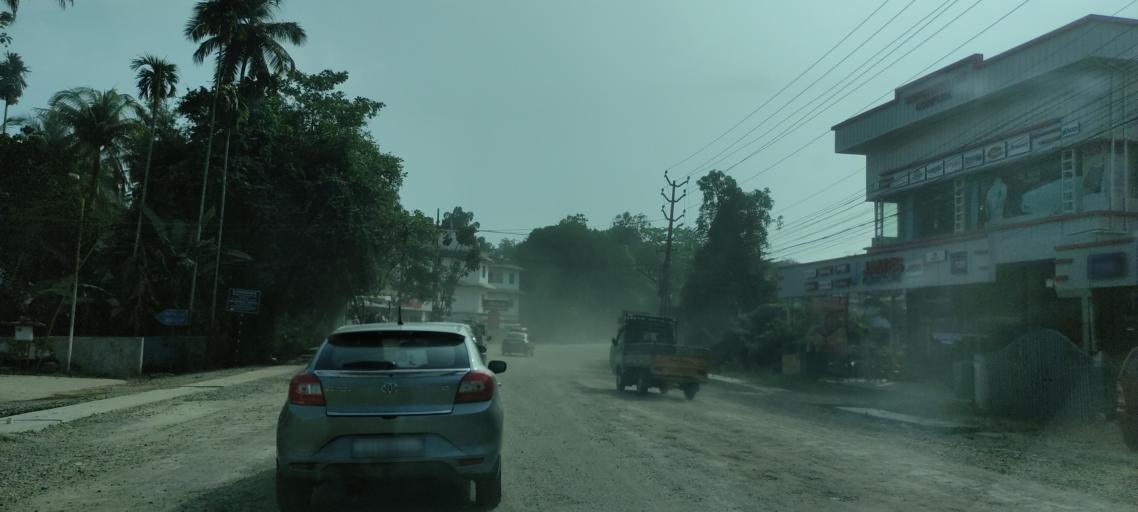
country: IN
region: Kerala
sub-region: Pattanamtitta
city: Tiruvalla
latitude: 9.3702
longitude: 76.5487
